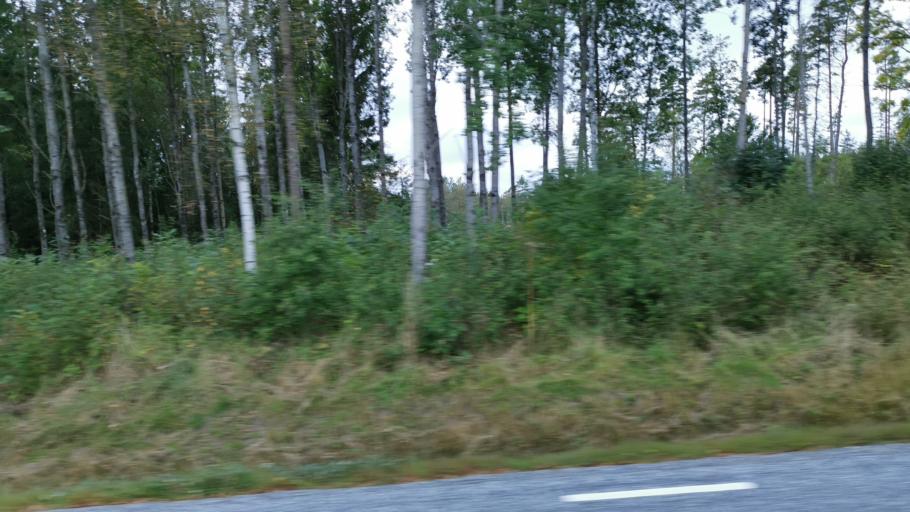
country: SE
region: Vaestra Goetaland
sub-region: Tanums Kommun
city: Tanumshede
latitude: 58.6916
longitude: 11.3355
